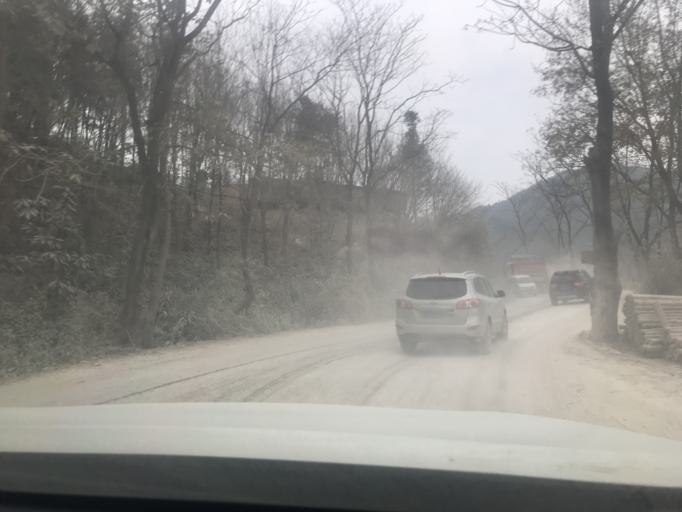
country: CN
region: Guangxi Zhuangzu Zizhiqu
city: Xinzhou
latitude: 25.0057
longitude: 105.8357
